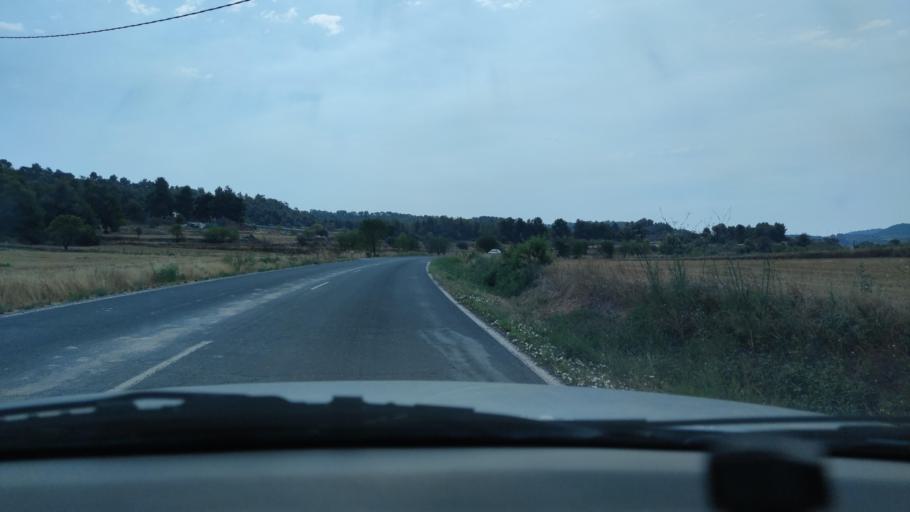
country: ES
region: Catalonia
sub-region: Provincia de Lleida
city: Fulleda
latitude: 41.5063
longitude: 0.9805
